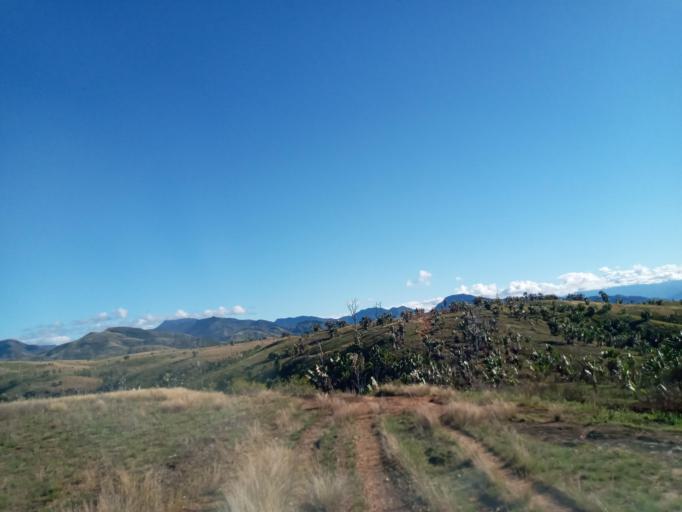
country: MG
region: Anosy
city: Fort Dauphin
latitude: -24.4063
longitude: 47.2485
